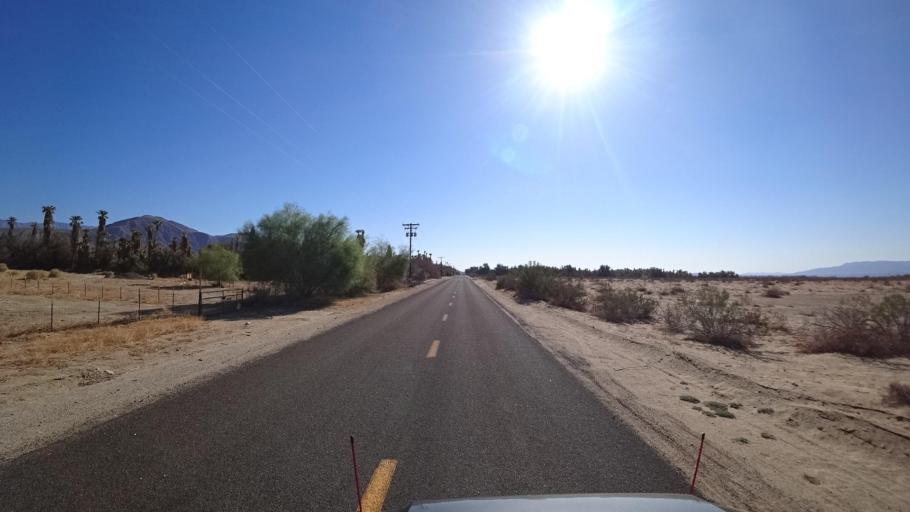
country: US
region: California
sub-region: San Diego County
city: Borrego Springs
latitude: 33.3016
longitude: -116.3809
